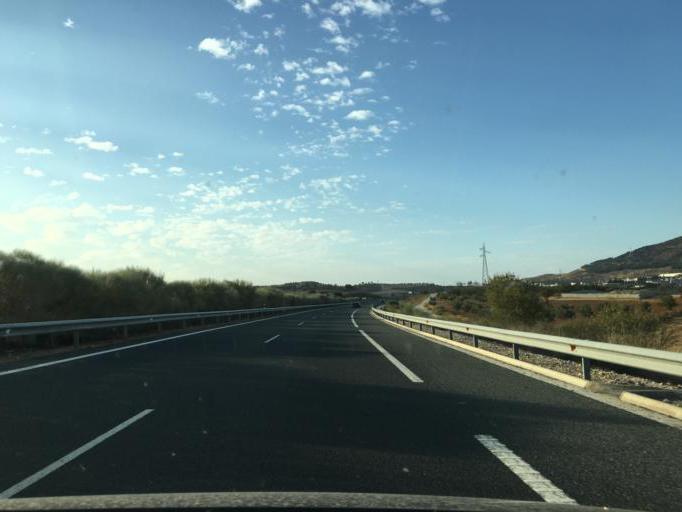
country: ES
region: Andalusia
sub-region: Provincia de Granada
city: Padul
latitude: 37.0235
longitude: -3.6442
